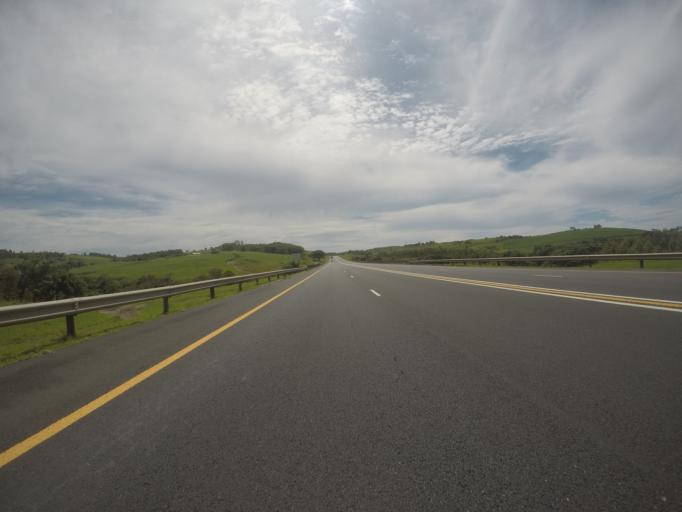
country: ZA
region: KwaZulu-Natal
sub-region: iLembe District Municipality
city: Mandeni
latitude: -29.1695
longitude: 31.5209
